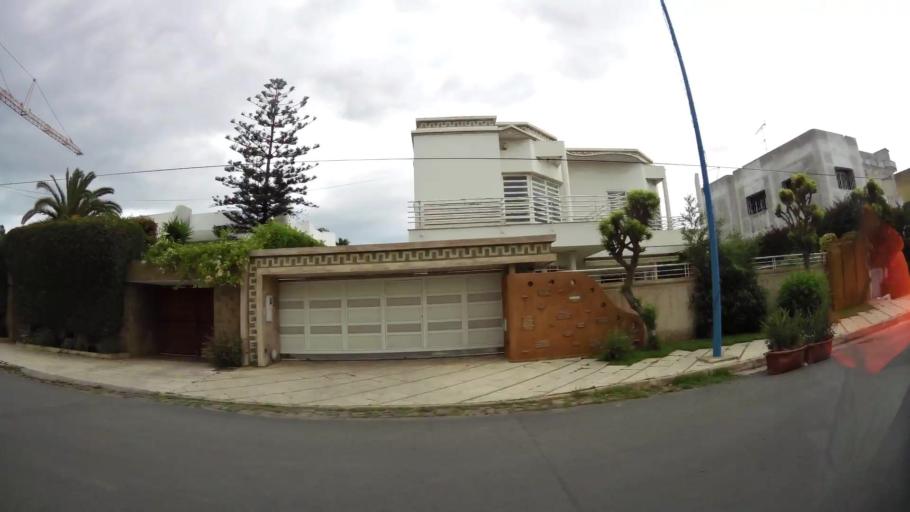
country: MA
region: Grand Casablanca
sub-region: Casablanca
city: Casablanca
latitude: 33.5643
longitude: -7.6415
